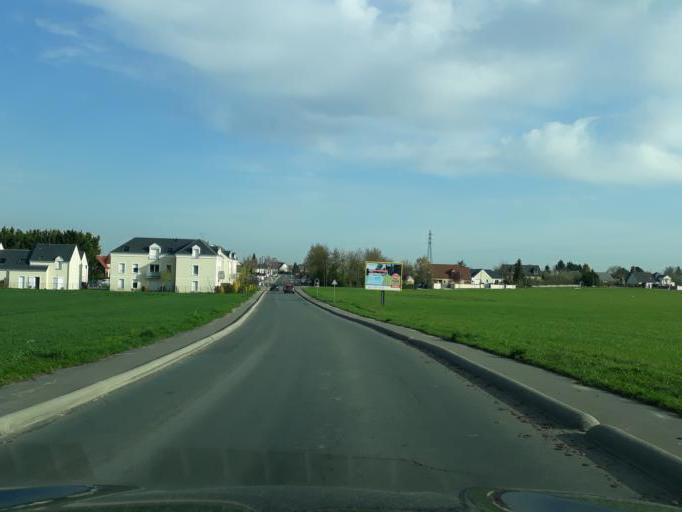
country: FR
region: Centre
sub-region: Departement du Loiret
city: La Chapelle-Saint-Mesmin
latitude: 47.9026
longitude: 1.8365
